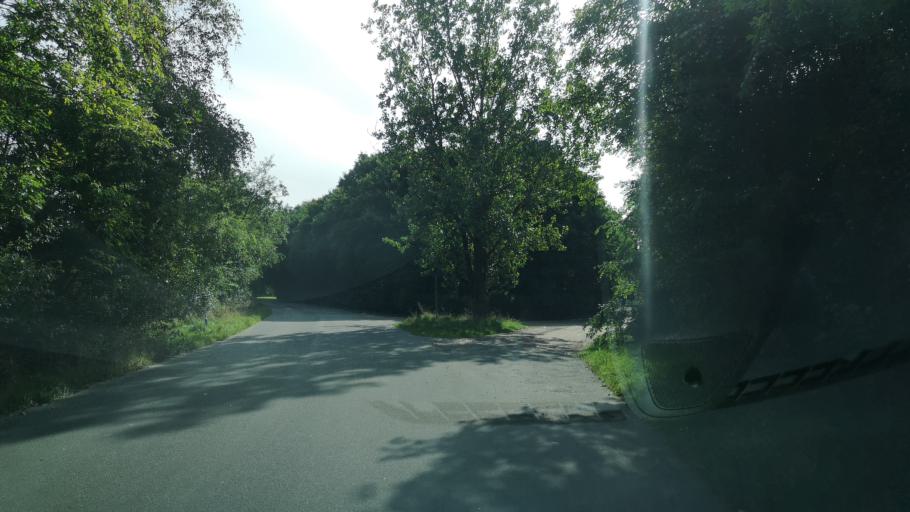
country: DK
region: Central Jutland
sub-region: Ikast-Brande Kommune
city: Ikast
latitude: 56.1507
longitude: 9.1332
